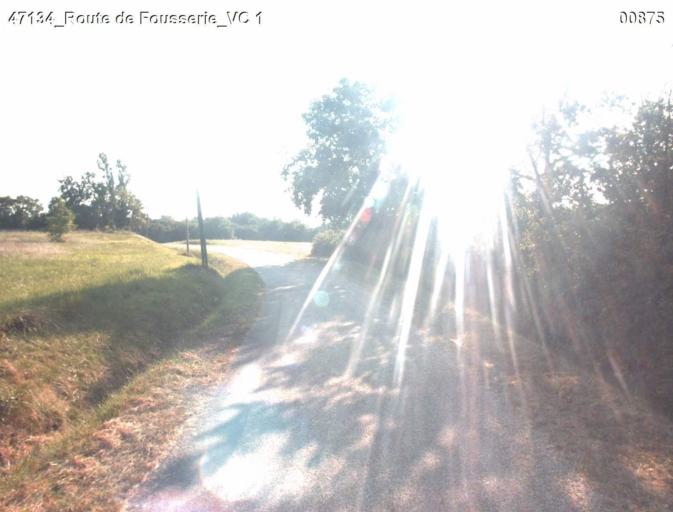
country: FR
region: Aquitaine
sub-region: Departement du Lot-et-Garonne
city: Mezin
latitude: 44.0267
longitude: 0.2791
